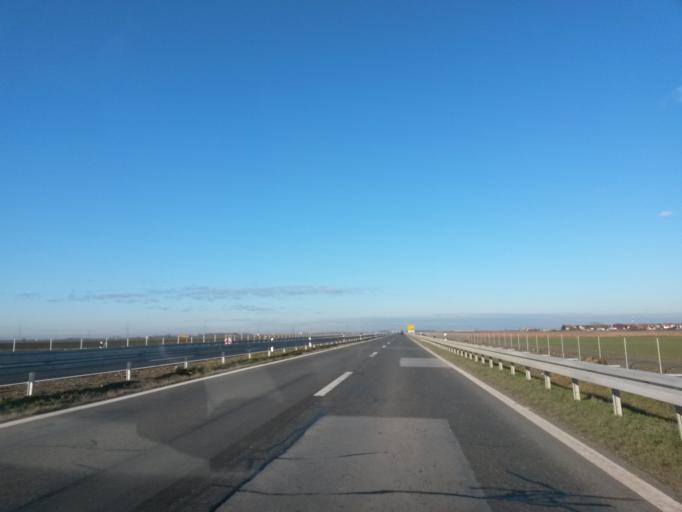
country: HR
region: Osjecko-Baranjska
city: Josipovac
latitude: 45.5656
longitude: 18.5898
